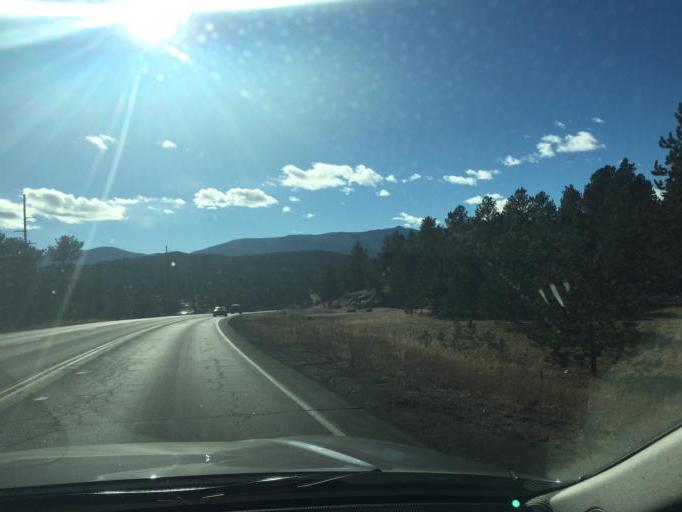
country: US
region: Colorado
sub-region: Jefferson County
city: Evergreen
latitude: 39.4480
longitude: -105.4413
